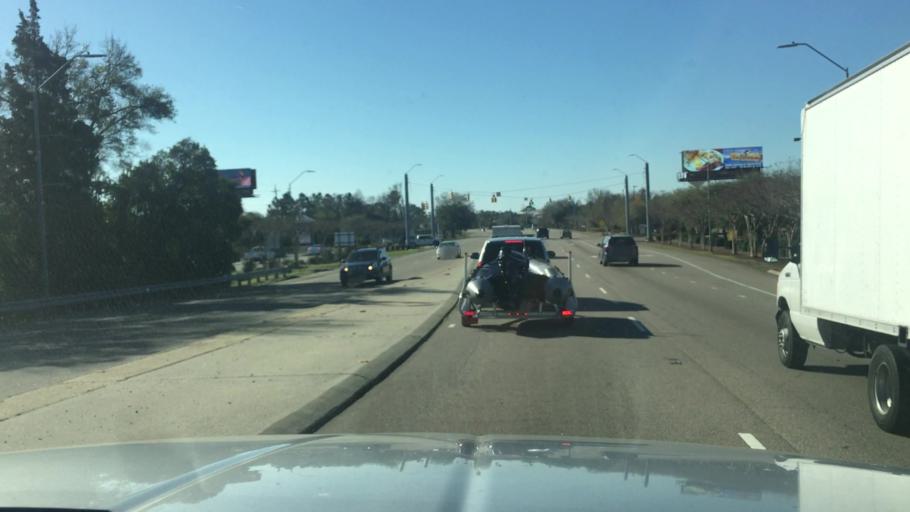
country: US
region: North Carolina
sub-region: New Hanover County
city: Sea Breeze
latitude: 34.0520
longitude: -77.8999
